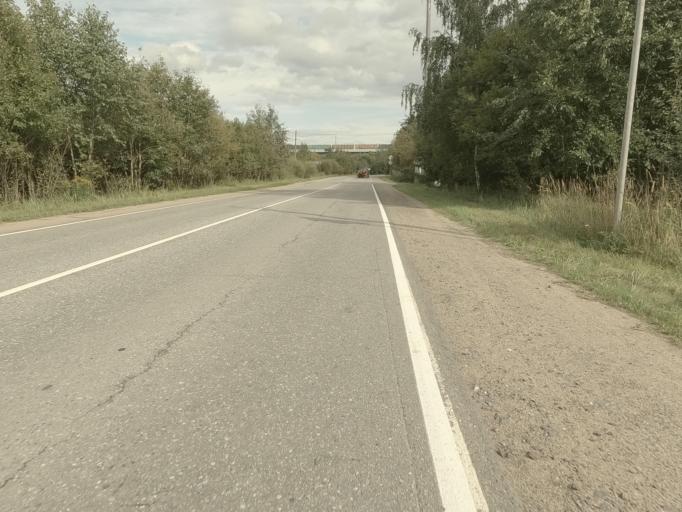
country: RU
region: Leningrad
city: Mga
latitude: 59.7603
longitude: 31.0133
